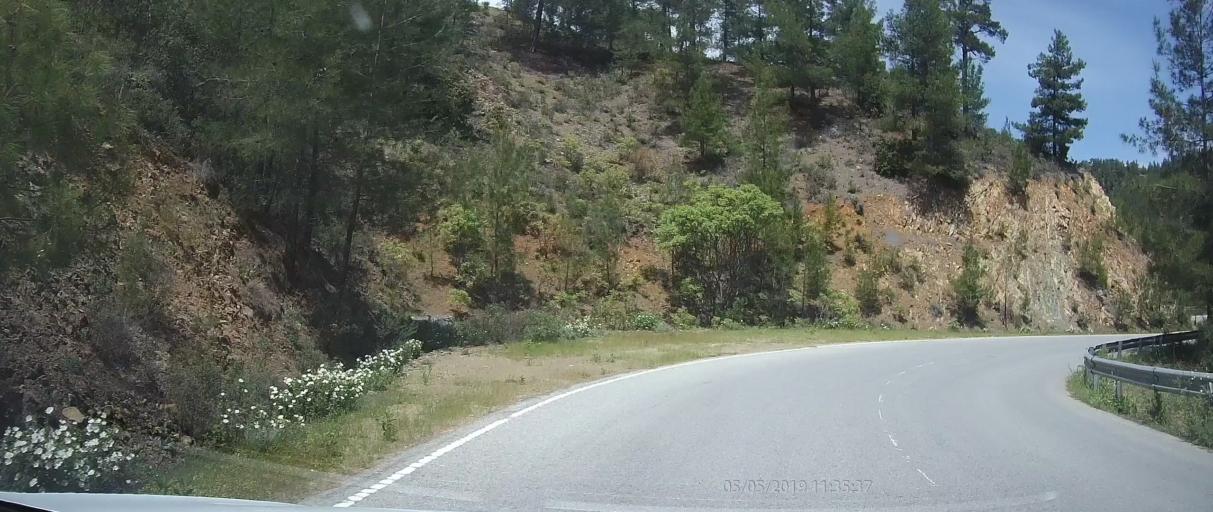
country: CY
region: Lefkosia
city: Kato Pyrgos
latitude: 34.9689
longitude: 32.6518
